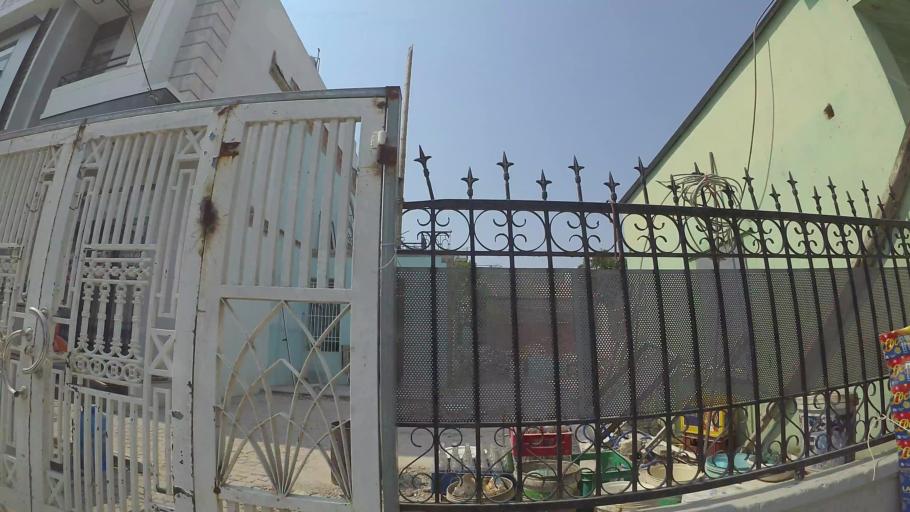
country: VN
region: Da Nang
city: Cam Le
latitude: 16.0101
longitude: 108.2000
